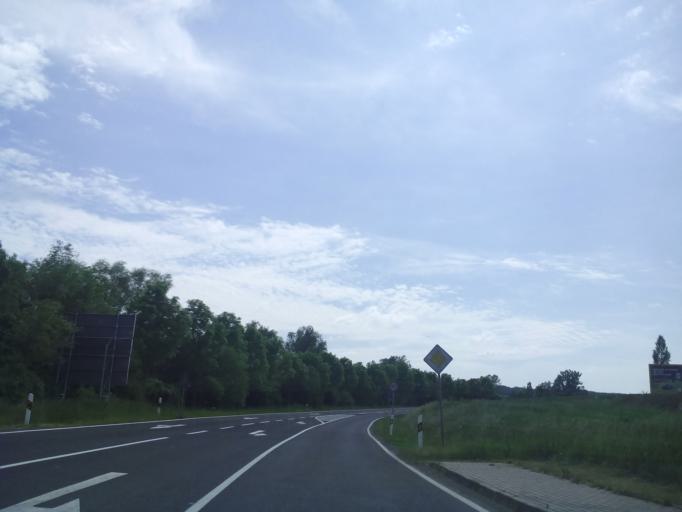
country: DE
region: Thuringia
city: Hellingen
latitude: 50.2750
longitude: 10.7286
